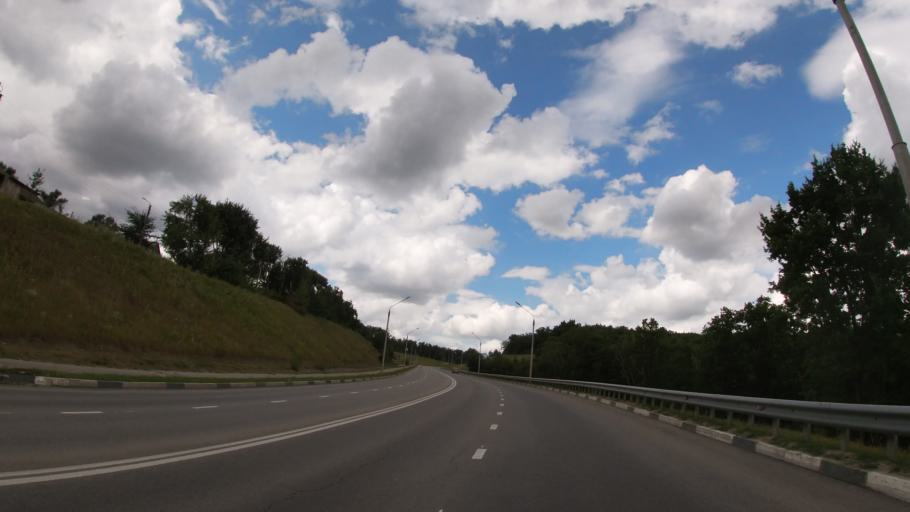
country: RU
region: Belgorod
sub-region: Belgorodskiy Rayon
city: Belgorod
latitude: 50.6207
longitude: 36.6158
